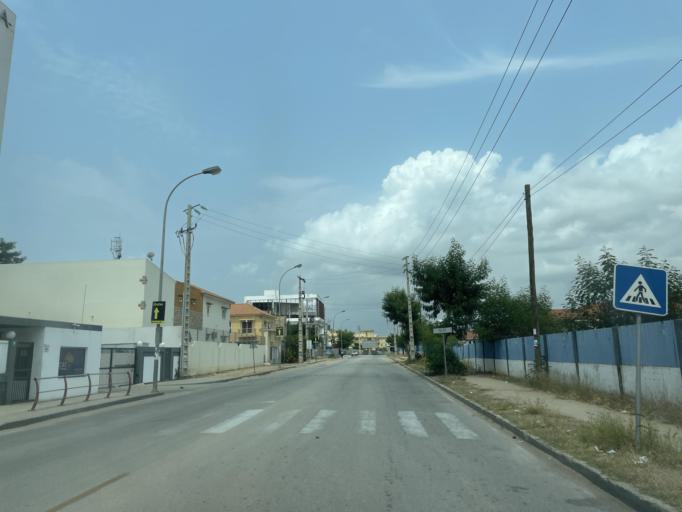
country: AO
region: Luanda
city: Luanda
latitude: -8.9237
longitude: 13.1943
